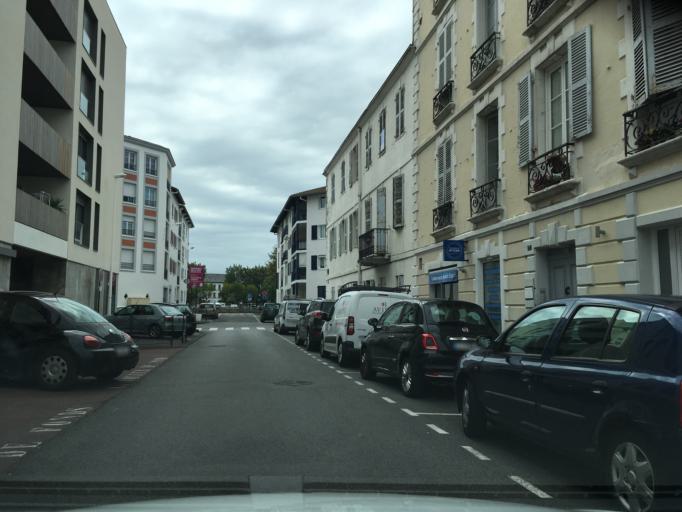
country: FR
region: Aquitaine
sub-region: Departement des Pyrenees-Atlantiques
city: Bayonne
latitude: 43.4941
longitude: -1.4680
